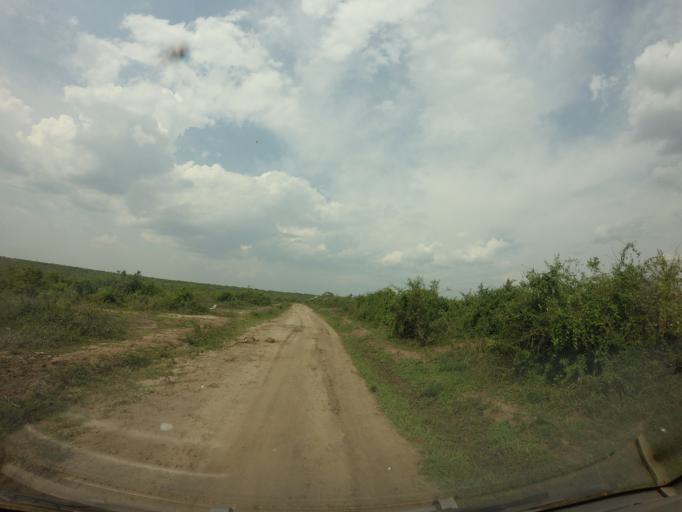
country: UG
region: Western Region
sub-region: Rubirizi District
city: Rubirizi
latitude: -0.2101
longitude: 29.9102
